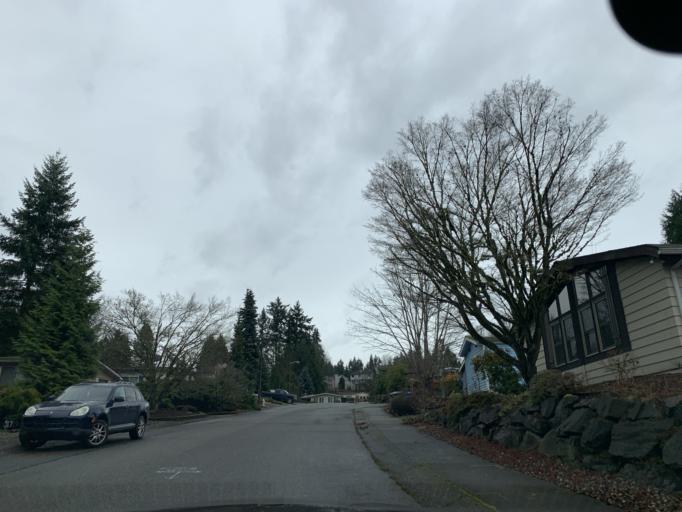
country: US
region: Washington
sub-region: King County
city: Woodinville
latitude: 47.7527
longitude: -122.1811
